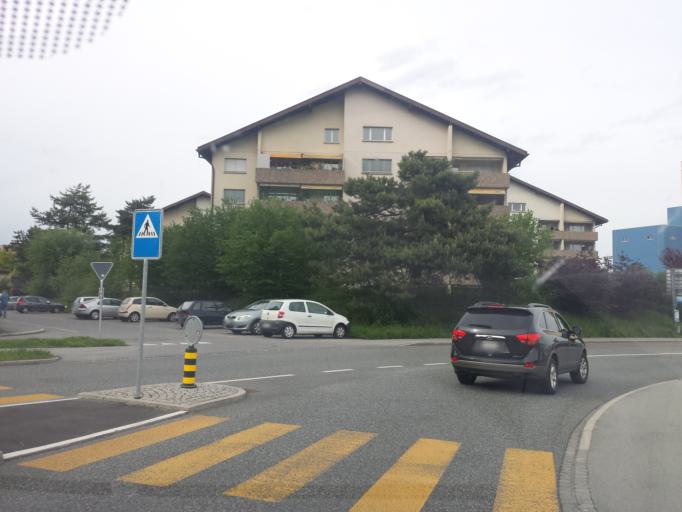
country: CH
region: Saint Gallen
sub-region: Wahlkreis Rheintal
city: Sankt Margrethen
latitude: 47.4462
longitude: 9.6483
